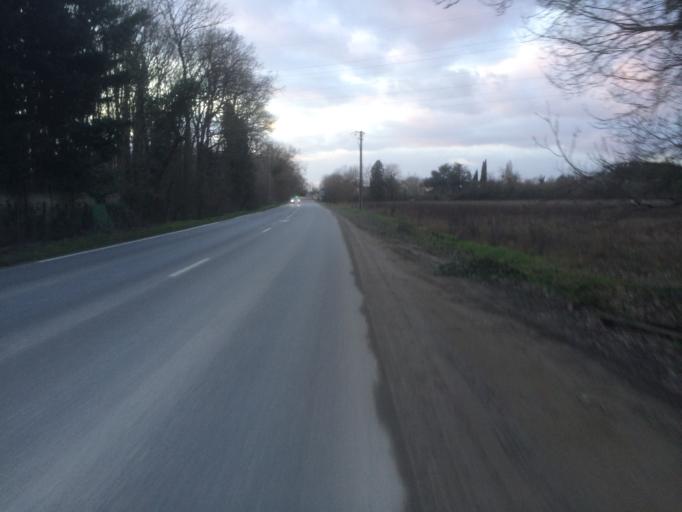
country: FR
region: Ile-de-France
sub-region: Departement de l'Essonne
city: Orsay
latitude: 48.6674
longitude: 2.2020
